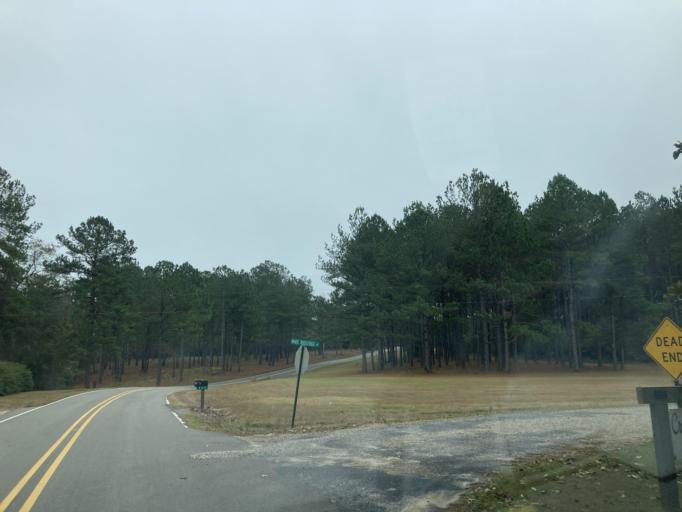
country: US
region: Mississippi
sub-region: Lamar County
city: Purvis
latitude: 31.0687
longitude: -89.4042
